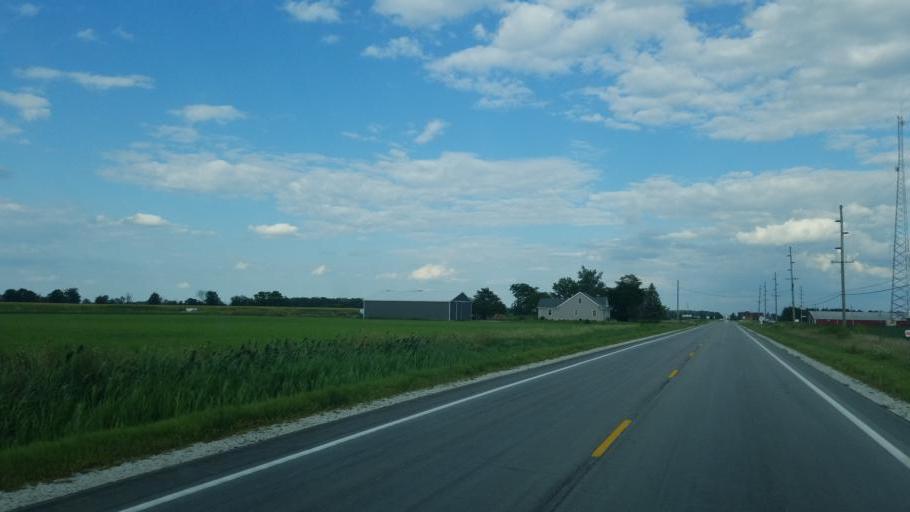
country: US
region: Ohio
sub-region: Sandusky County
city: Gibsonburg
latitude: 41.3413
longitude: -83.2772
